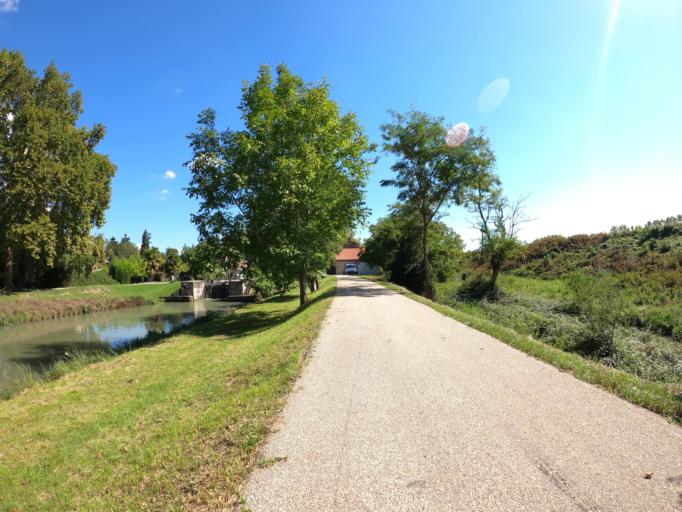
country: FR
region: Midi-Pyrenees
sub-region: Departement du Tarn-et-Garonne
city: Valence
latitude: 44.1038
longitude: 0.9000
